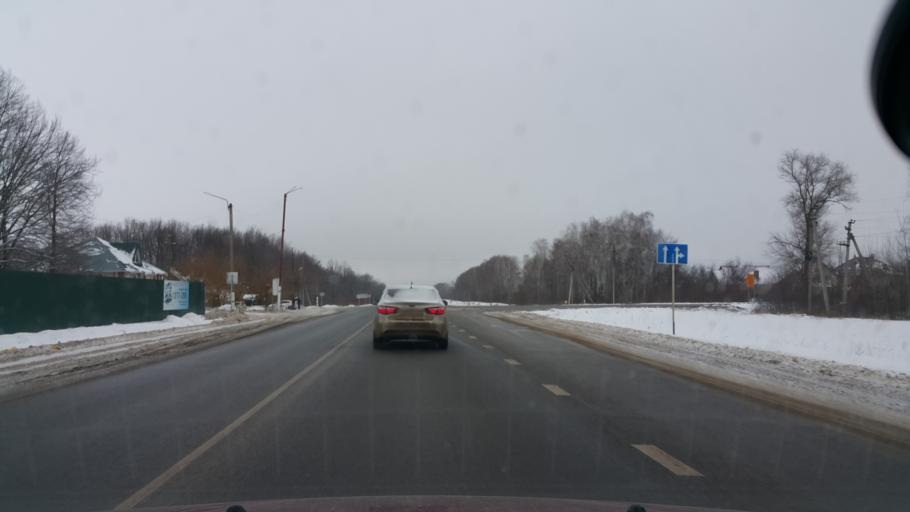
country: RU
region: Tambov
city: Bokino
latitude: 52.6158
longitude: 41.4438
